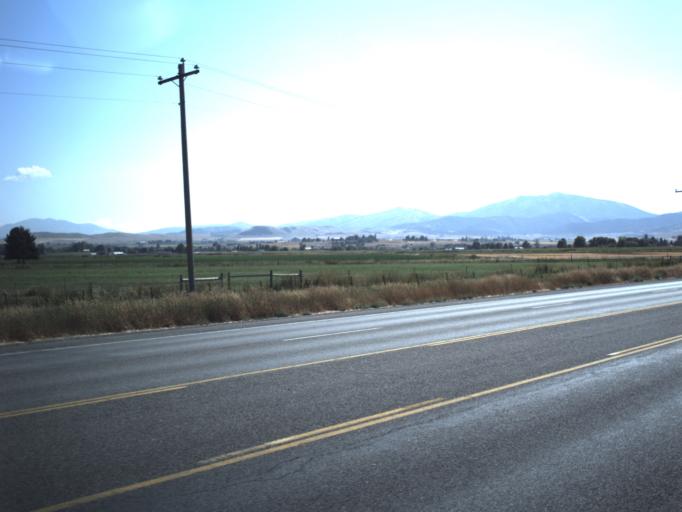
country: US
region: Utah
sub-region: Cache County
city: Wellsville
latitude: 41.6561
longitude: -111.9027
